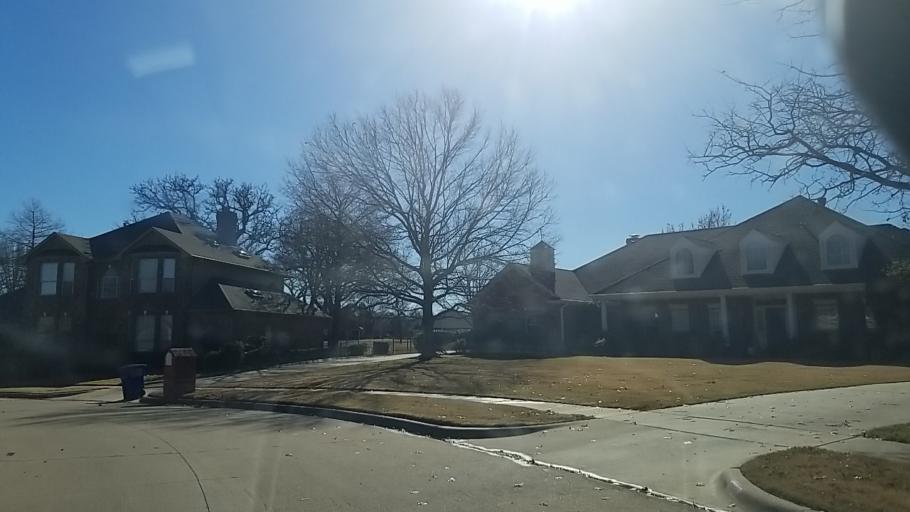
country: US
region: Texas
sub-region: Denton County
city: Corinth
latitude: 33.1574
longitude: -97.0858
